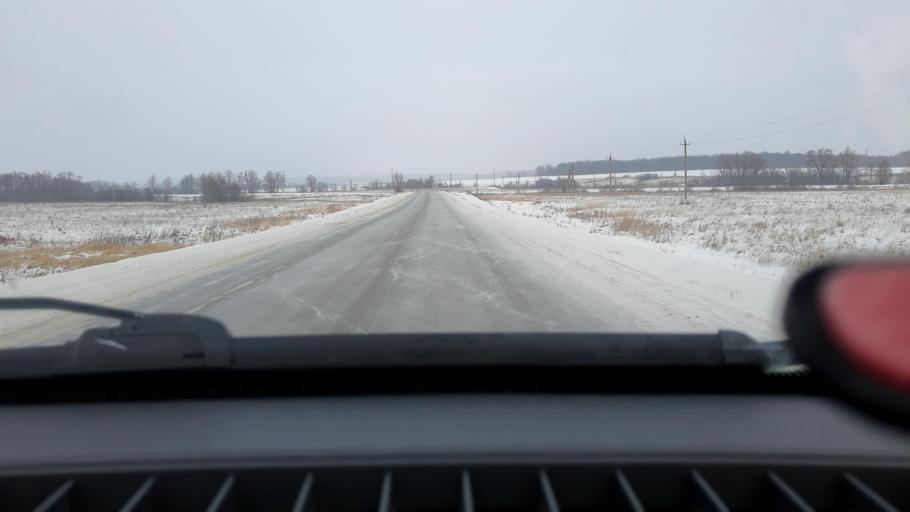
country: RU
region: Bashkortostan
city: Iglino
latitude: 54.7239
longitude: 56.4049
